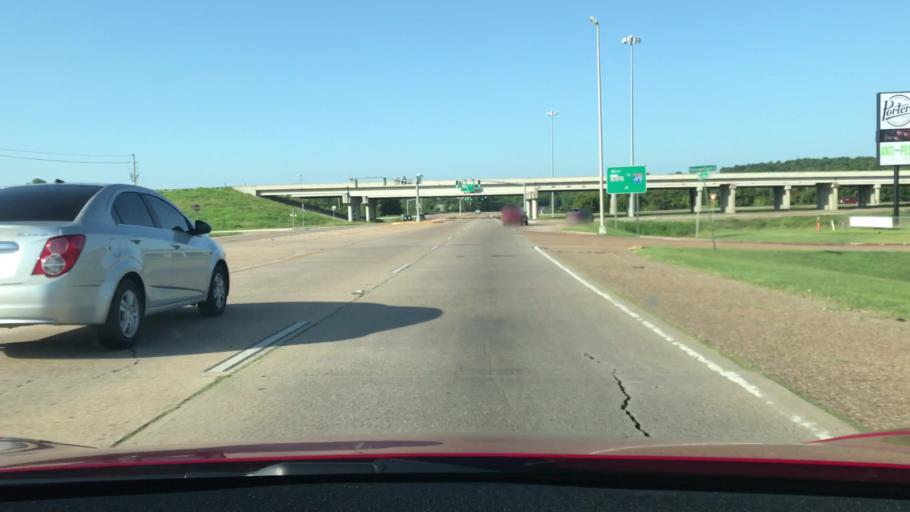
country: US
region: Louisiana
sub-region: Bossier Parish
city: Bossier City
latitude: 32.4133
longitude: -93.7242
